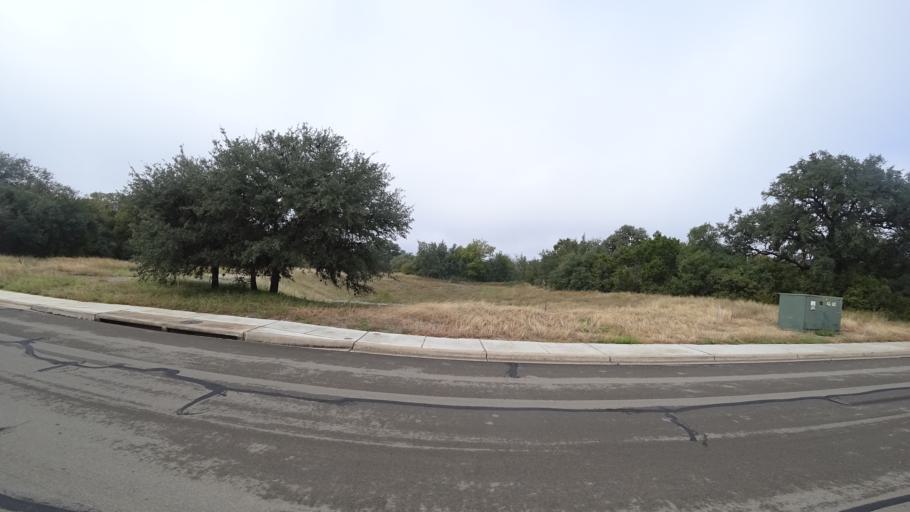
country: US
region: Texas
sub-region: Travis County
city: Shady Hollow
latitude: 30.1884
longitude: -97.8716
